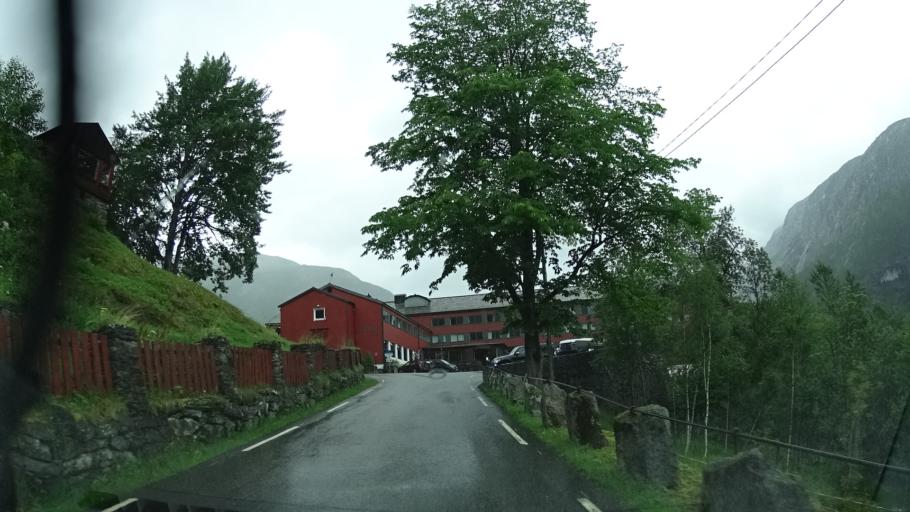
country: NO
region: Sogn og Fjordane
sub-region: Vik
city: Vik
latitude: 60.8346
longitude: 6.6802
